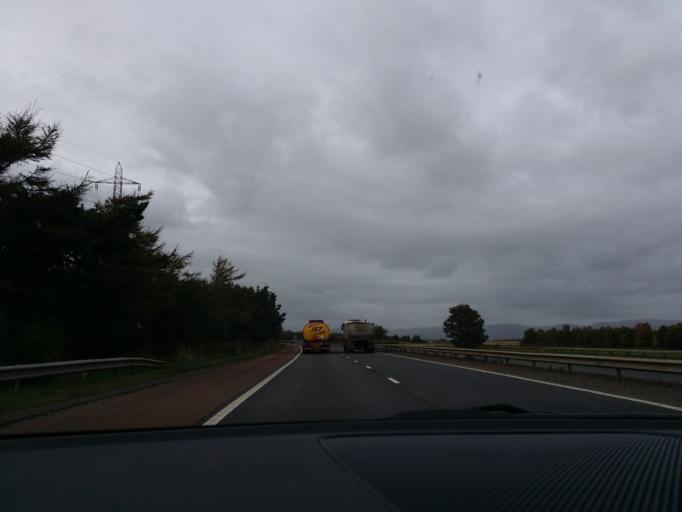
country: GB
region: Scotland
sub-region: Falkirk
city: Airth
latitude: 56.0344
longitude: -3.7675
